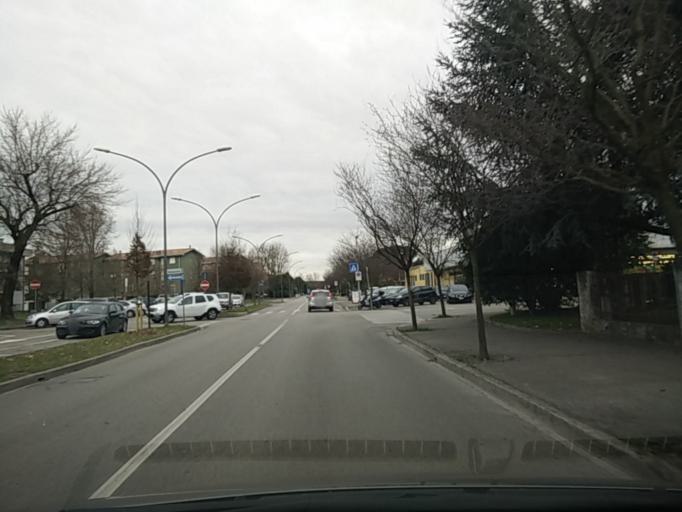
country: IT
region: Veneto
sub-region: Provincia di Treviso
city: Treviso
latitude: 45.6544
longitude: 12.2301
